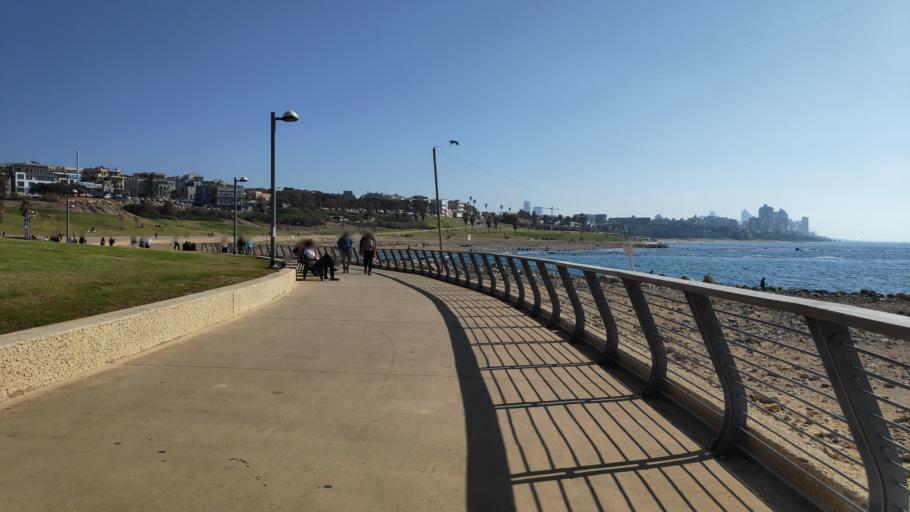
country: IL
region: Tel Aviv
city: Yafo
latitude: 32.0454
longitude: 34.7450
